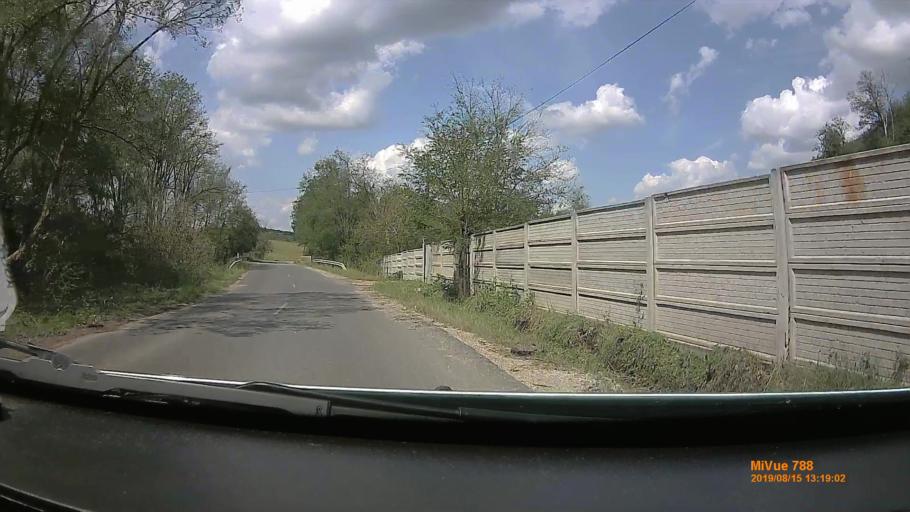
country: HU
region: Borsod-Abauj-Zemplen
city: Kazincbarcika
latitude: 48.1729
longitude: 20.6336
